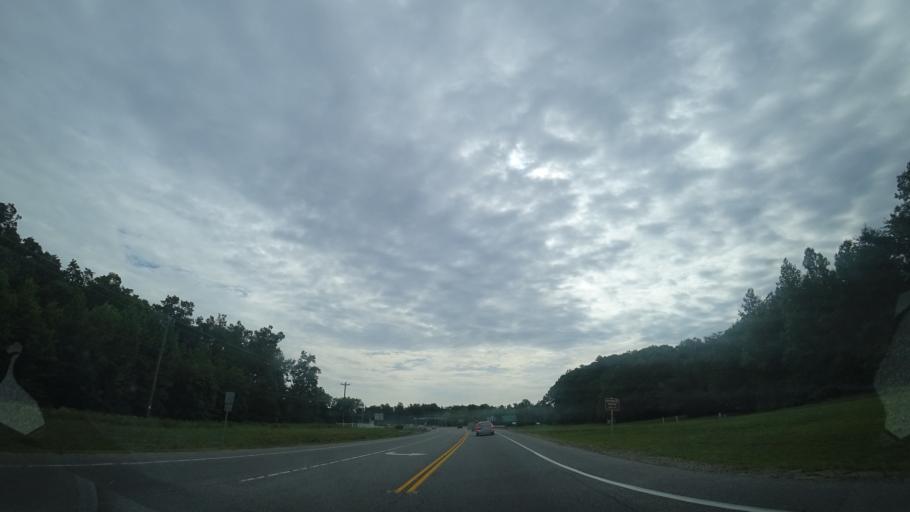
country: US
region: Virginia
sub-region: Spotsylvania County
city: Spotsylvania Courthouse
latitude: 38.1622
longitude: -77.6454
